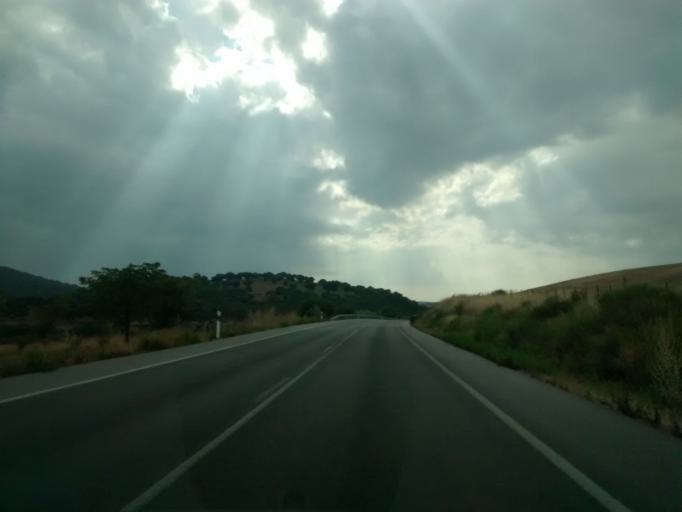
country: ES
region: Andalusia
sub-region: Provincia de Cadiz
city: Prado del Rey
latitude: 36.7522
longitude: -5.5965
